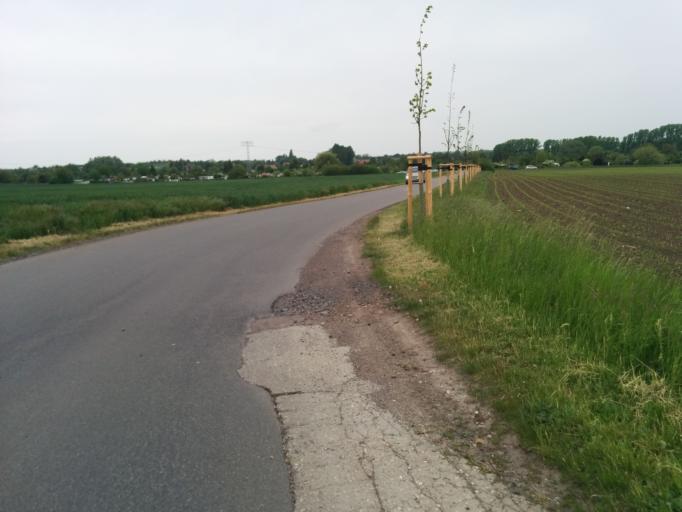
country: DE
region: Saxony-Anhalt
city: Zscherben
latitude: 51.4579
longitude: 11.8760
